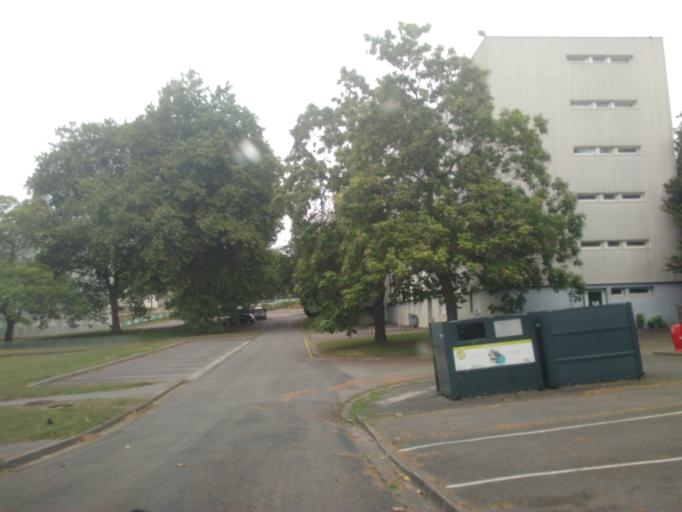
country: FR
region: Brittany
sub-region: Departement d'Ille-et-Vilaine
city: Cesson-Sevigne
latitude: 48.1224
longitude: -1.6345
